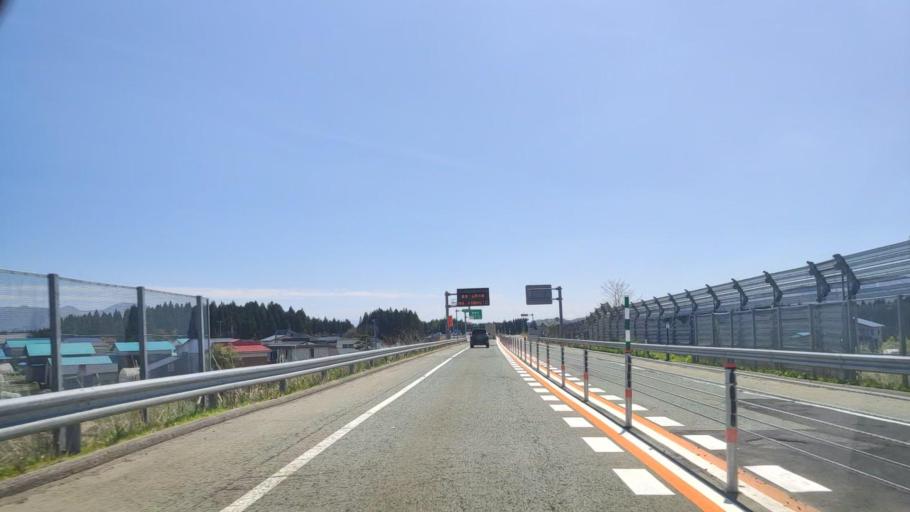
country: JP
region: Yamagata
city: Obanazawa
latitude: 38.6397
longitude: 140.3732
